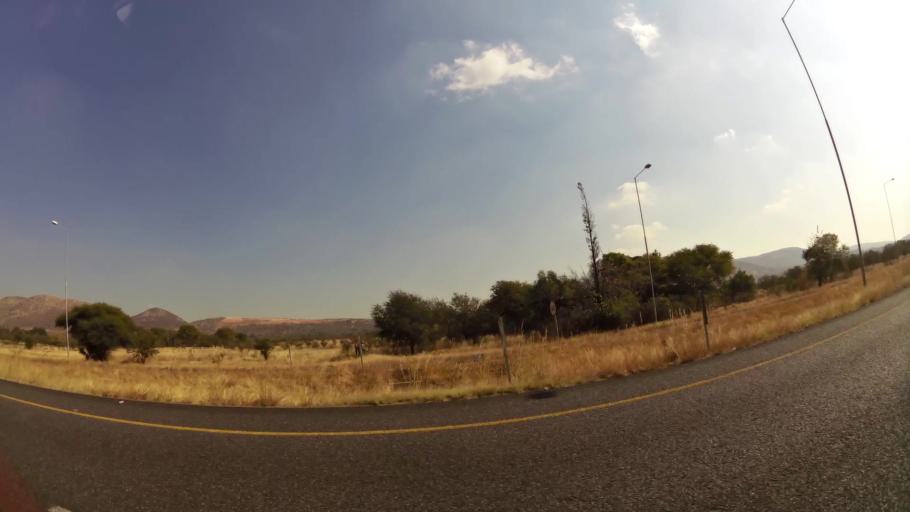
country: ZA
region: North-West
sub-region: Bojanala Platinum District Municipality
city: Rustenburg
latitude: -25.6181
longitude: 27.1551
